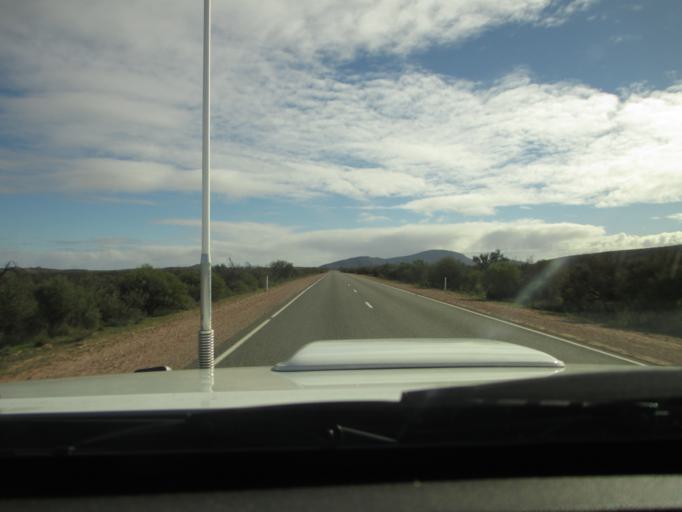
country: AU
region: South Australia
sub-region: Flinders Ranges
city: Quorn
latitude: -31.8477
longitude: 138.3950
